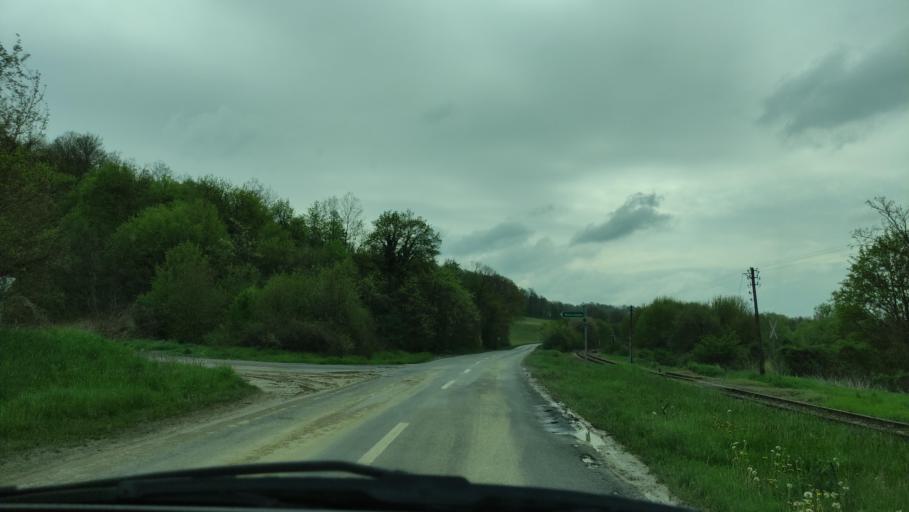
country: HU
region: Baranya
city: Komlo
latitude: 46.2196
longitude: 18.2393
